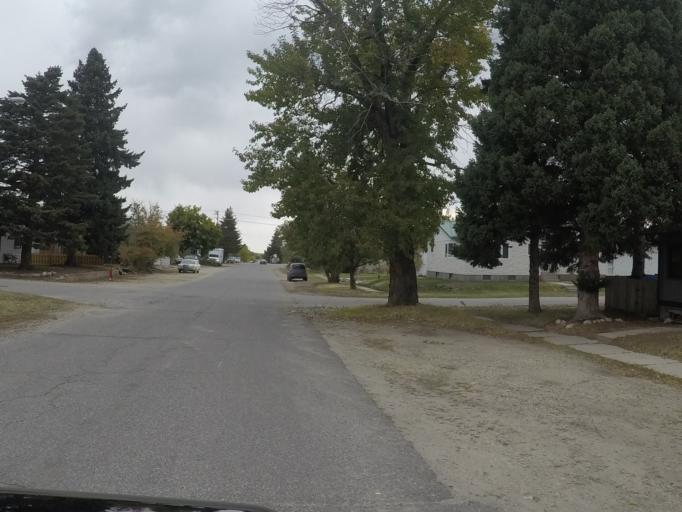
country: US
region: Montana
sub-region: Carbon County
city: Red Lodge
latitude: 45.1906
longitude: -109.2445
